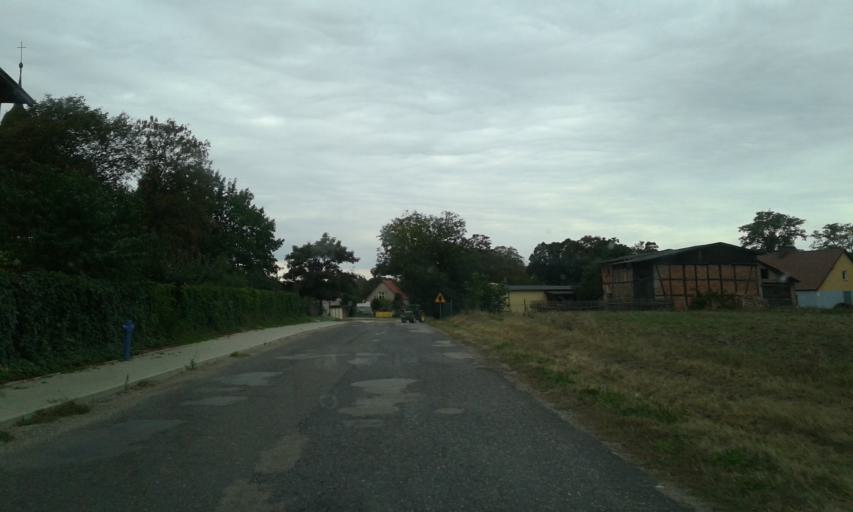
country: PL
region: West Pomeranian Voivodeship
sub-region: Powiat pyrzycki
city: Warnice
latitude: 53.1854
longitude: 15.0174
